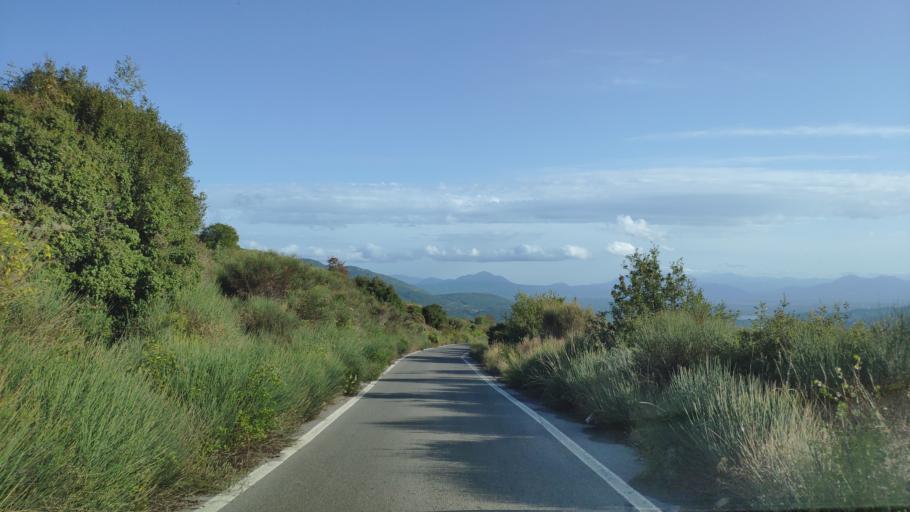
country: GR
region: Peloponnese
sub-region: Nomos Arkadias
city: Dimitsana
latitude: 37.5638
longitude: 22.0294
